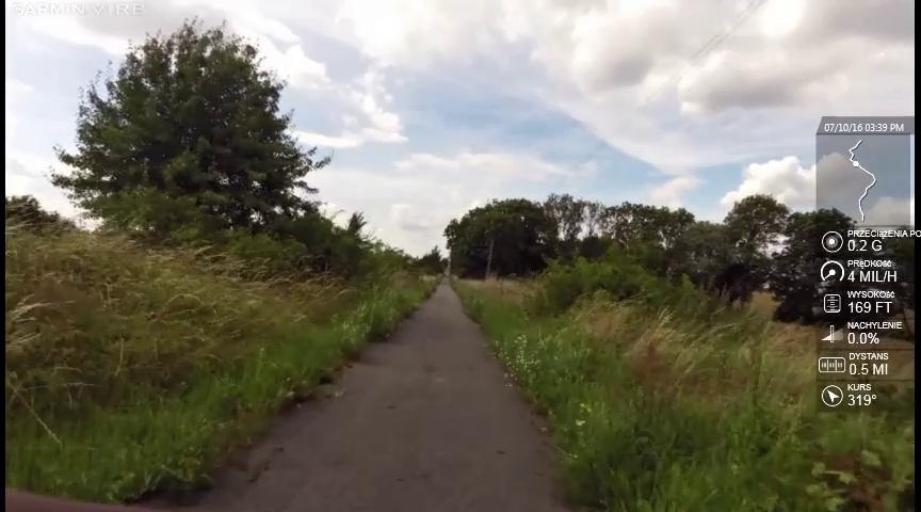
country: PL
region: West Pomeranian Voivodeship
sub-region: Powiat gryfinski
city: Banie
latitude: 53.1198
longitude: 14.6220
